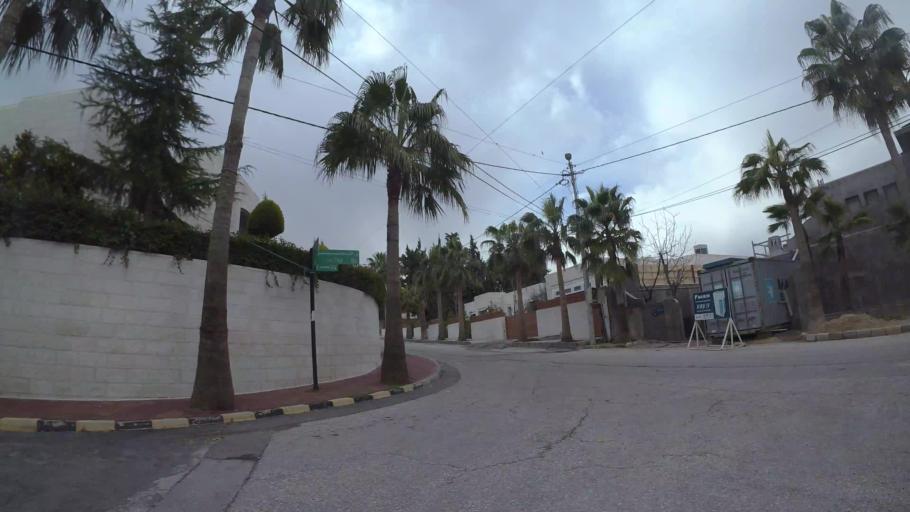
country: JO
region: Amman
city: Wadi as Sir
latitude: 31.9890
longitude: 35.8216
